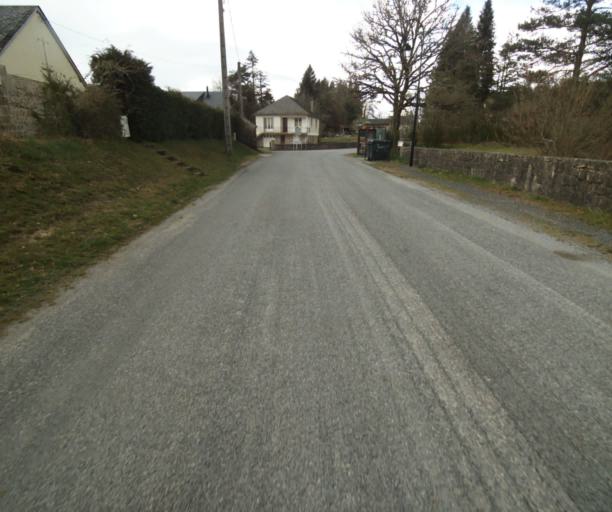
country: FR
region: Limousin
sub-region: Departement de la Correze
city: Correze
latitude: 45.2792
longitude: 1.9770
